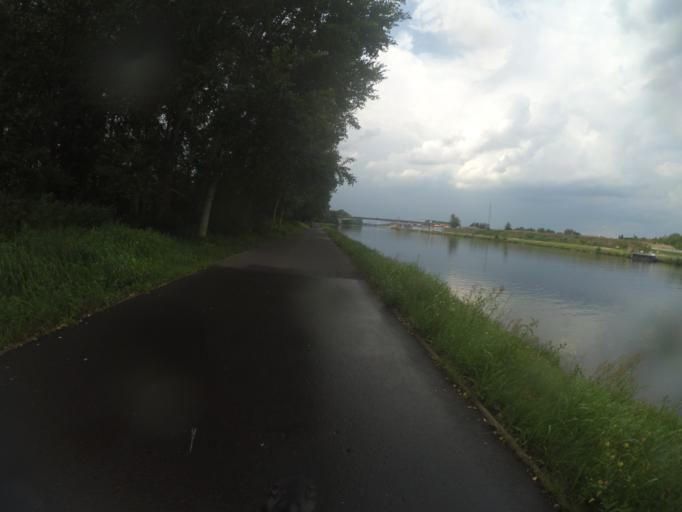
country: CZ
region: Central Bohemia
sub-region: Okres Melnik
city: Melnik
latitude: 50.3531
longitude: 14.4658
